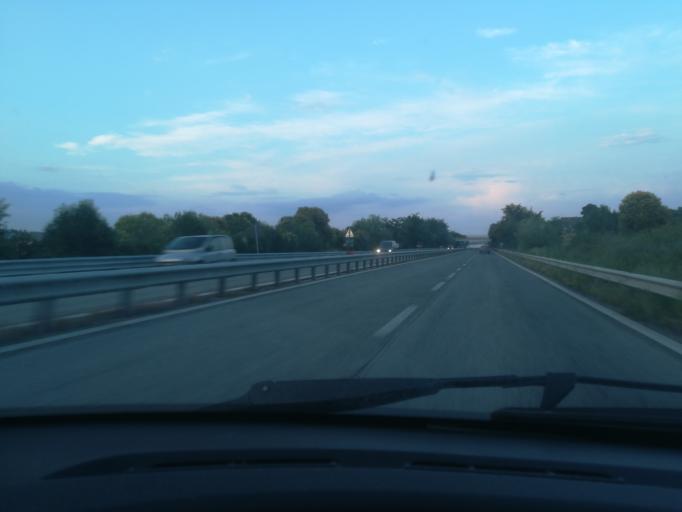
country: IT
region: The Marches
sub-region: Provincia di Macerata
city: Sforzacosta
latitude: 43.2456
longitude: 13.4246
